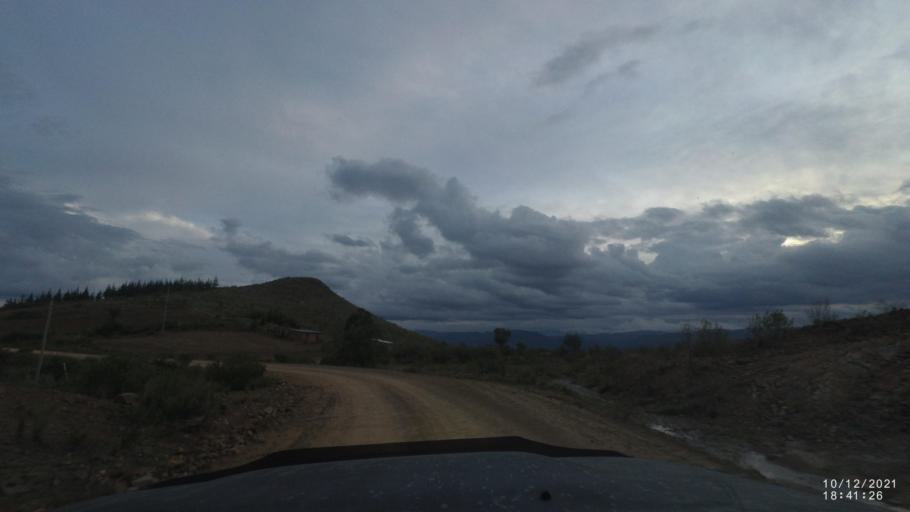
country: BO
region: Cochabamba
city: Tarata
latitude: -17.8627
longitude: -65.9890
